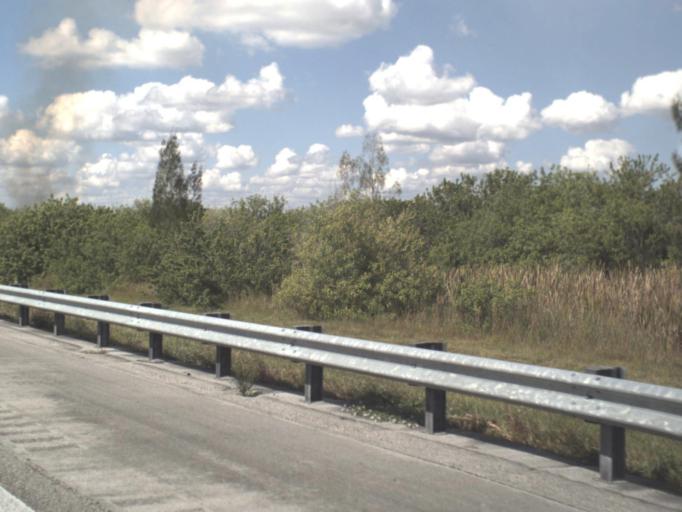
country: US
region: Florida
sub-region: Saint Lucie County
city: Lakewood Park
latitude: 27.4852
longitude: -80.5294
